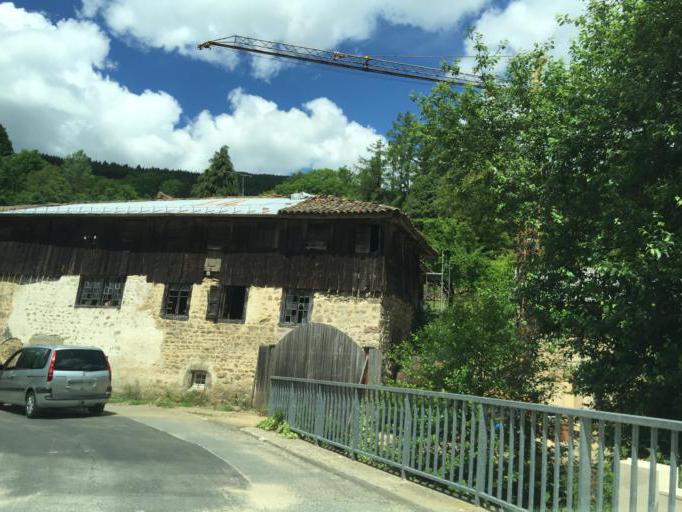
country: FR
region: Auvergne
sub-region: Departement du Puy-de-Dome
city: Ambert
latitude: 45.5393
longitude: 3.7977
